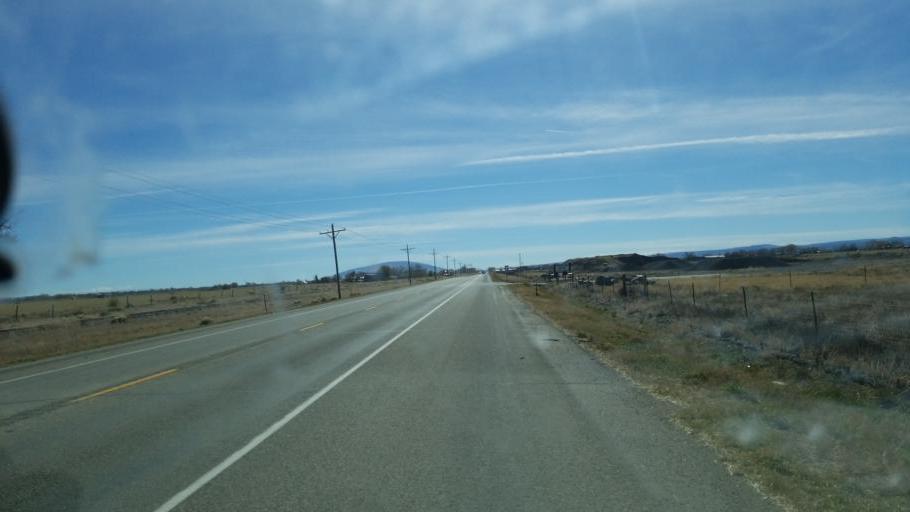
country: US
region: Colorado
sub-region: Conejos County
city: Conejos
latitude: 37.1589
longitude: -105.9919
